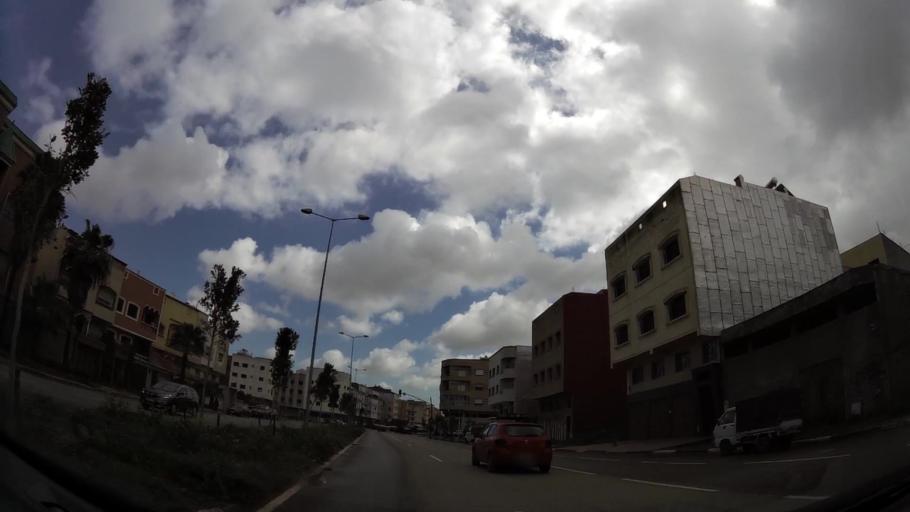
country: MA
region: Grand Casablanca
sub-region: Casablanca
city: Casablanca
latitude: 33.5321
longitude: -7.5856
